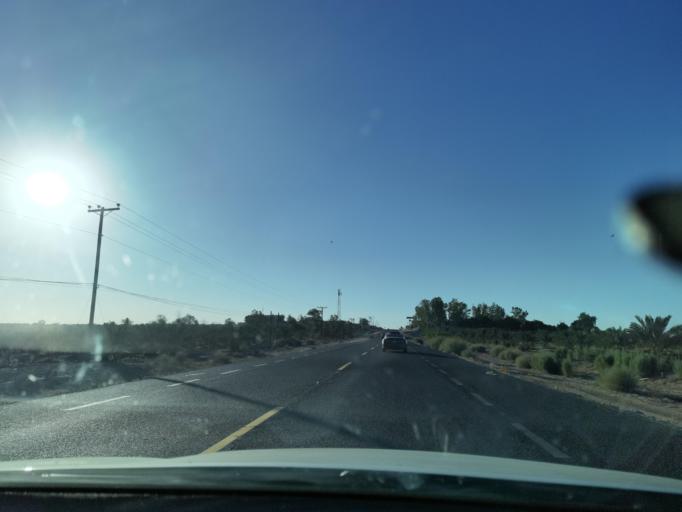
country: MX
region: Baja California
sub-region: Mexicali
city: Islas Agrarias Grupo A
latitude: 32.6416
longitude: -115.3045
